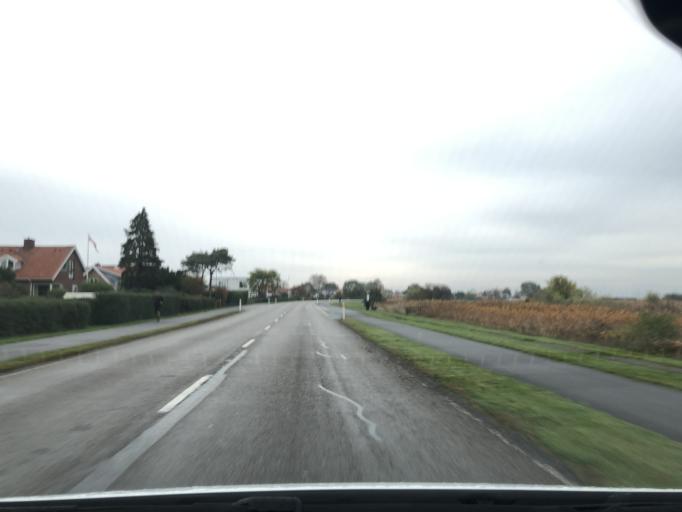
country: DK
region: Capital Region
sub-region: Dragor Kommune
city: Dragor
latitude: 55.5868
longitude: 12.6648
